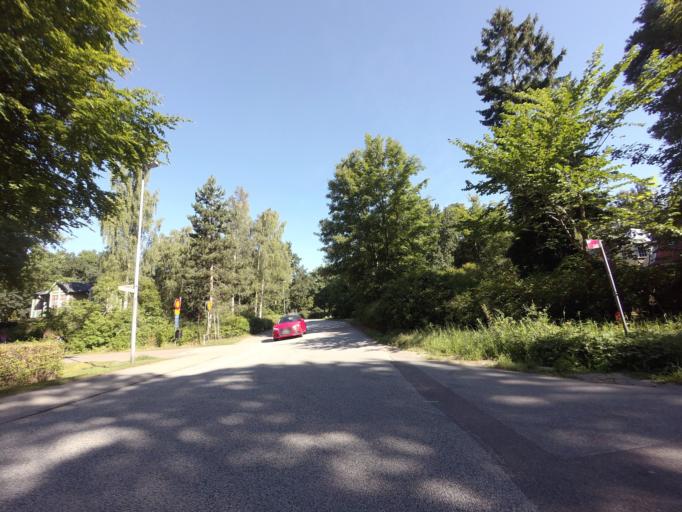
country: SE
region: Skane
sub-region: Ystads Kommun
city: Ystad
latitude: 55.4282
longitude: 13.8490
